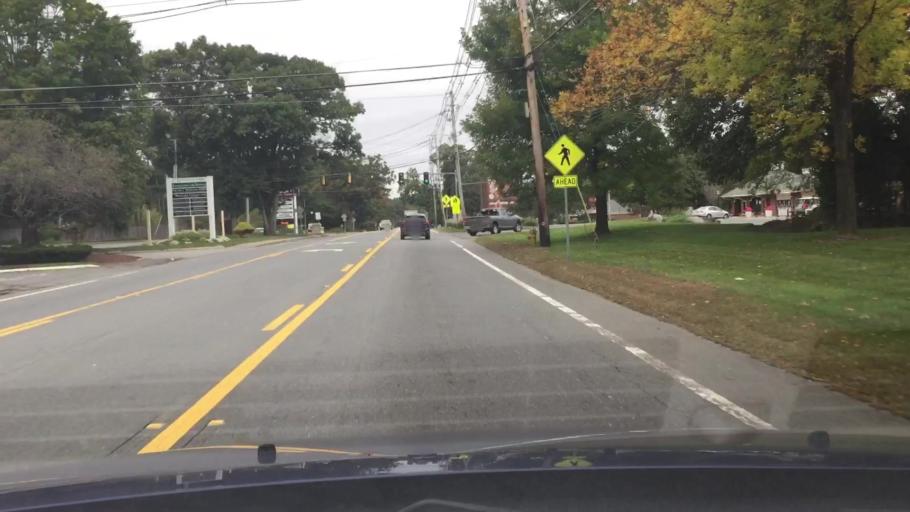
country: US
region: Massachusetts
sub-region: Essex County
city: Middleton
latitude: 42.5833
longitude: -71.0054
